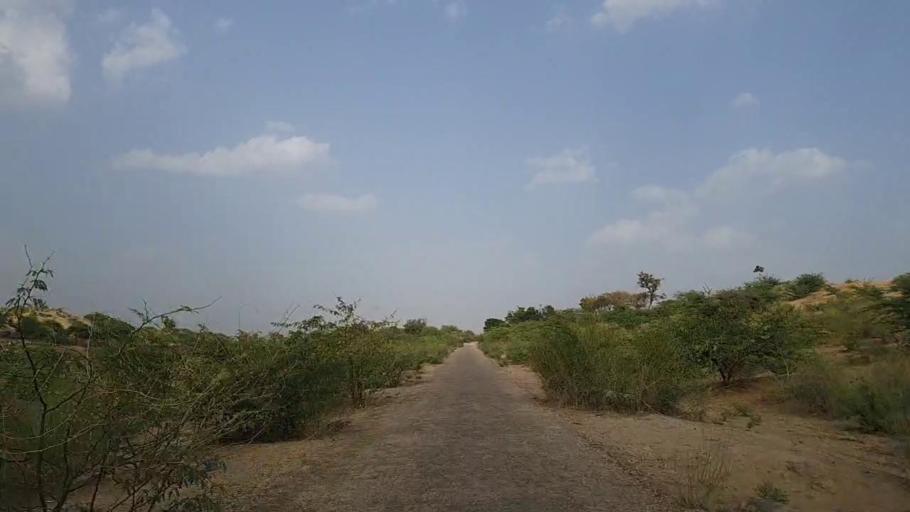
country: PK
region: Sindh
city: Islamkot
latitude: 24.7727
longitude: 70.1827
